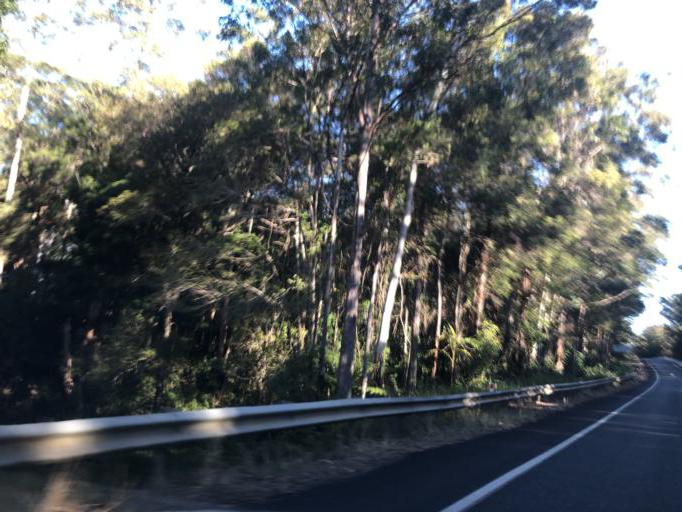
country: AU
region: New South Wales
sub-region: Nambucca Shire
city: Nambucca
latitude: -30.5519
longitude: 153.0081
